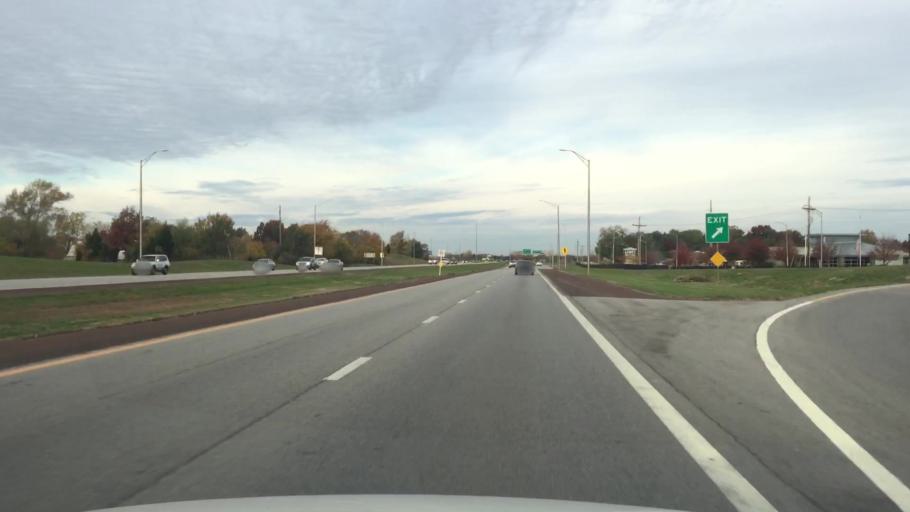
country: US
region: Kansas
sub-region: Johnson County
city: Shawnee
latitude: 39.0087
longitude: -94.7713
